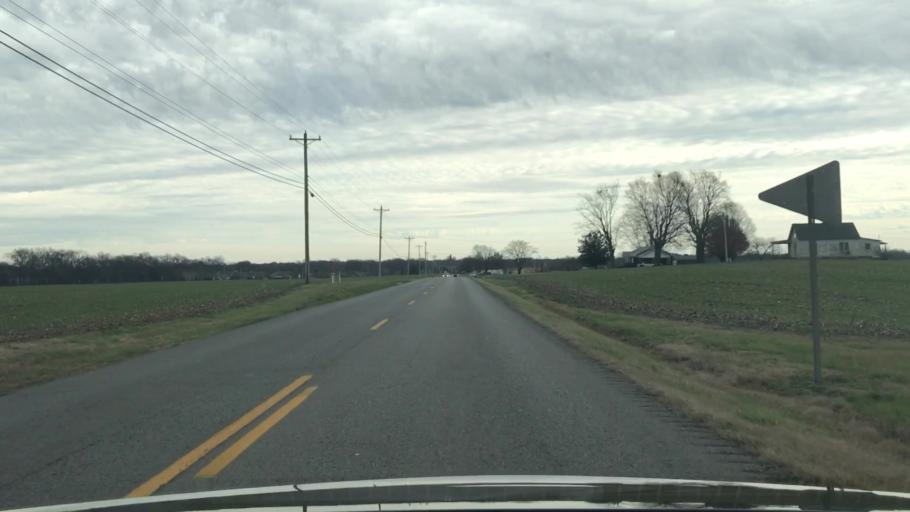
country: US
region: Kentucky
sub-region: Christian County
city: Hopkinsville
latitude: 36.8620
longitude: -87.5340
